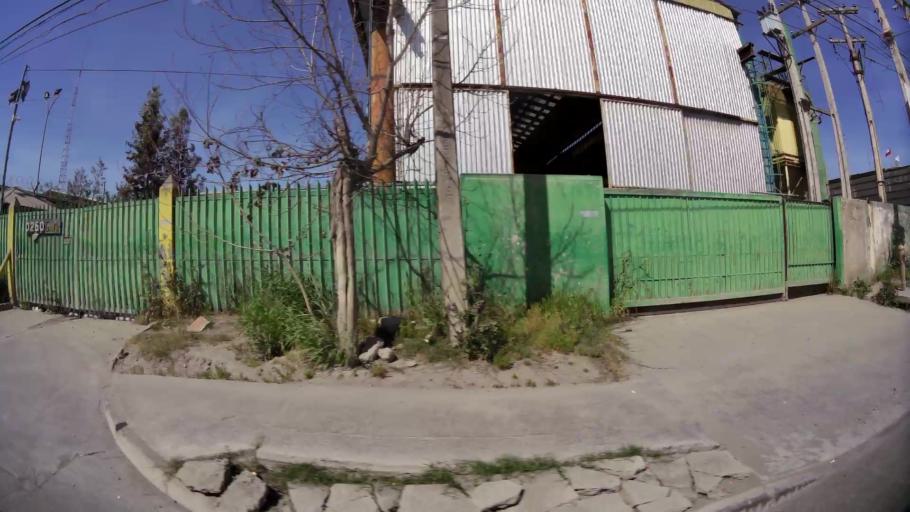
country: CL
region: Santiago Metropolitan
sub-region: Provincia de Maipo
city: San Bernardo
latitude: -33.5385
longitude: -70.6940
